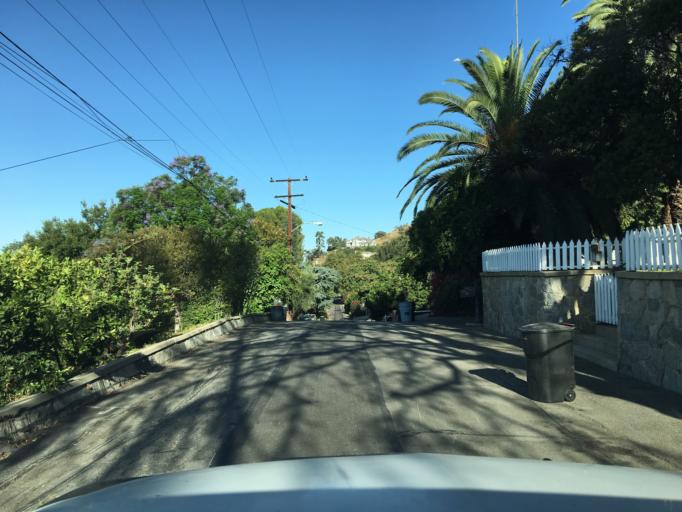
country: US
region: California
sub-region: Los Angeles County
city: Glendora
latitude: 34.1478
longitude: -117.8850
